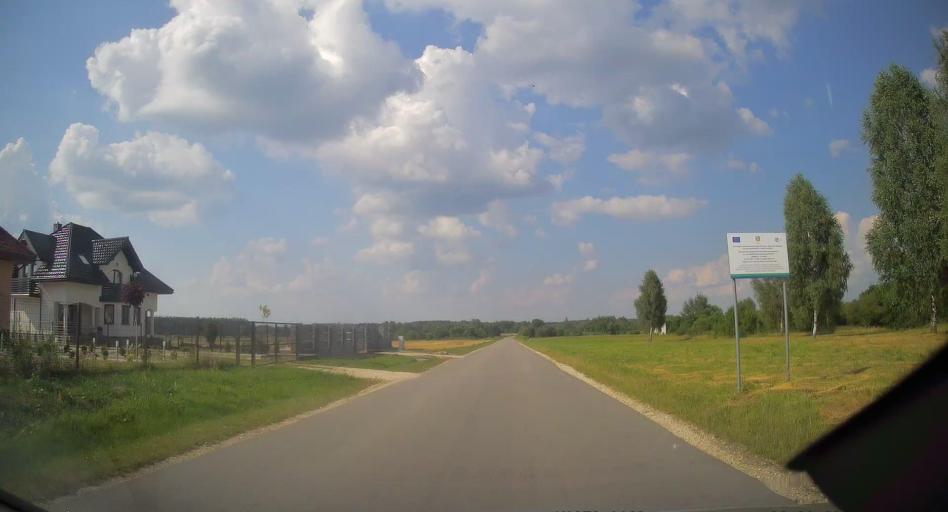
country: PL
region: Swietokrzyskie
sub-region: Powiat konecki
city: Radoszyce
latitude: 51.0851
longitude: 20.2583
